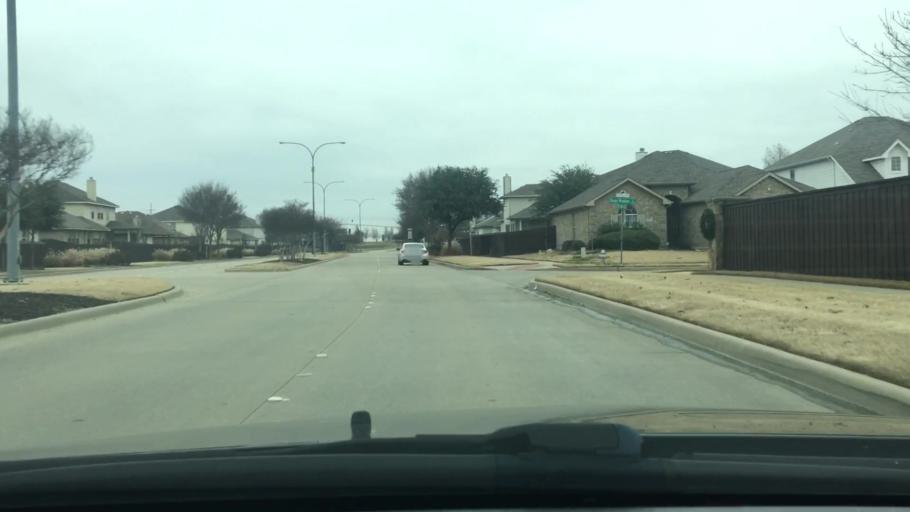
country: US
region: Texas
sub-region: Tarrant County
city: Keller
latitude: 32.9686
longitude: -97.2624
